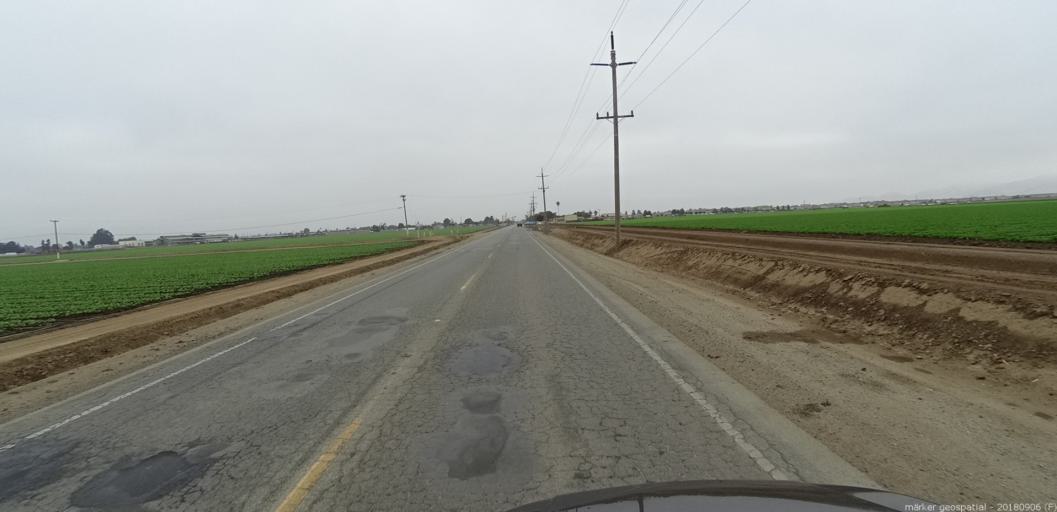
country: US
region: California
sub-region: Monterey County
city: Salinas
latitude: 36.6680
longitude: -121.5968
